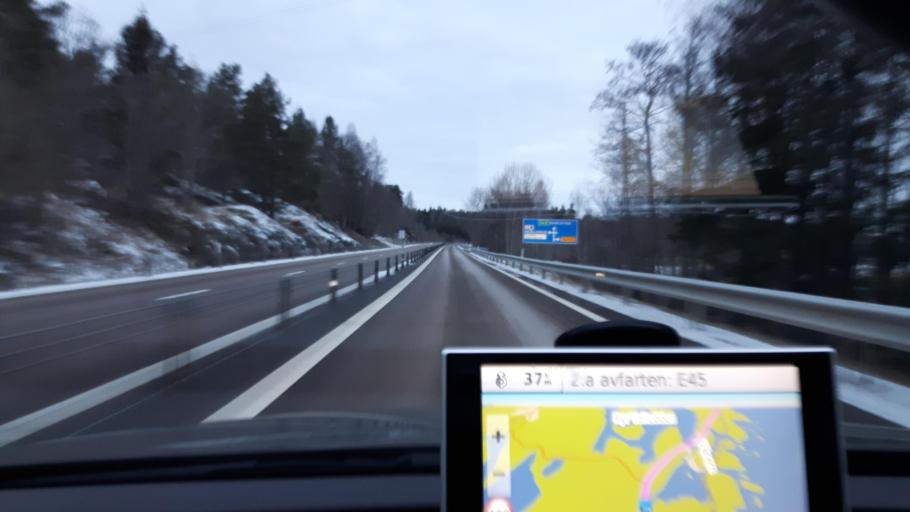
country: SE
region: Vaestra Goetaland
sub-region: Melleruds Kommun
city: Mellerud
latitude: 58.7599
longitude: 12.4903
